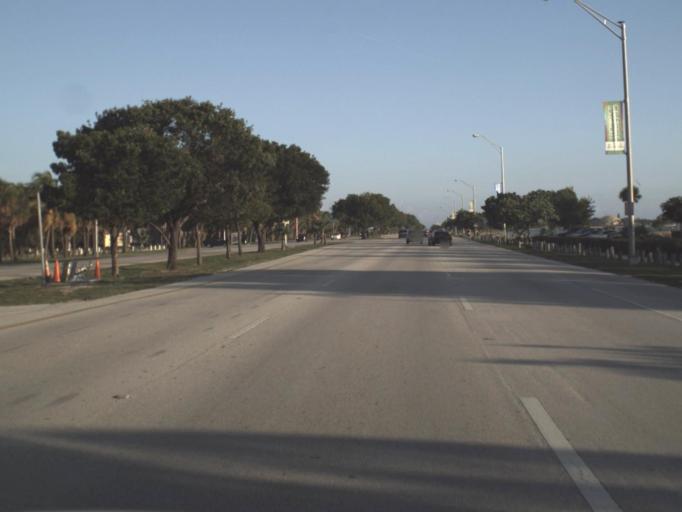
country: US
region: Florida
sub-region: Miami-Dade County
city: Miami
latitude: 25.7455
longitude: -80.1757
